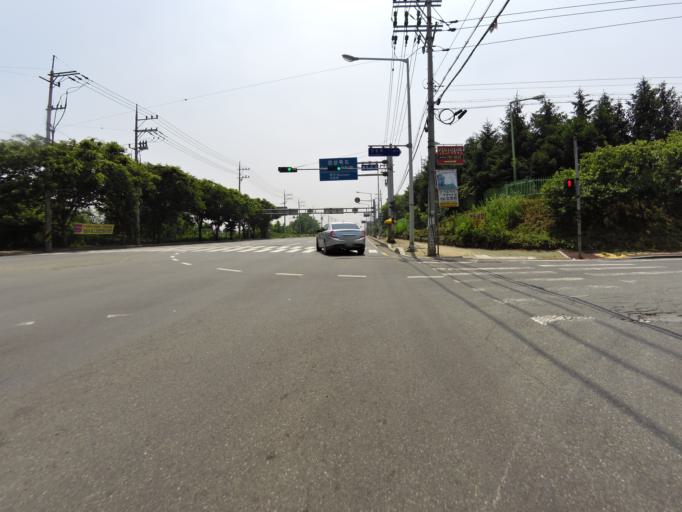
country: KR
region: Gyeongsangbuk-do
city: Gyeongsan-si
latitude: 35.8535
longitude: 128.7251
